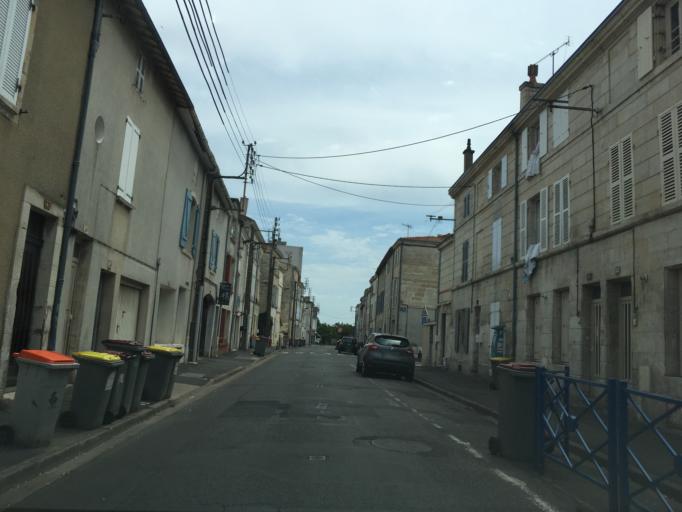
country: FR
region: Poitou-Charentes
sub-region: Departement des Deux-Sevres
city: Niort
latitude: 46.3198
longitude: -0.4587
